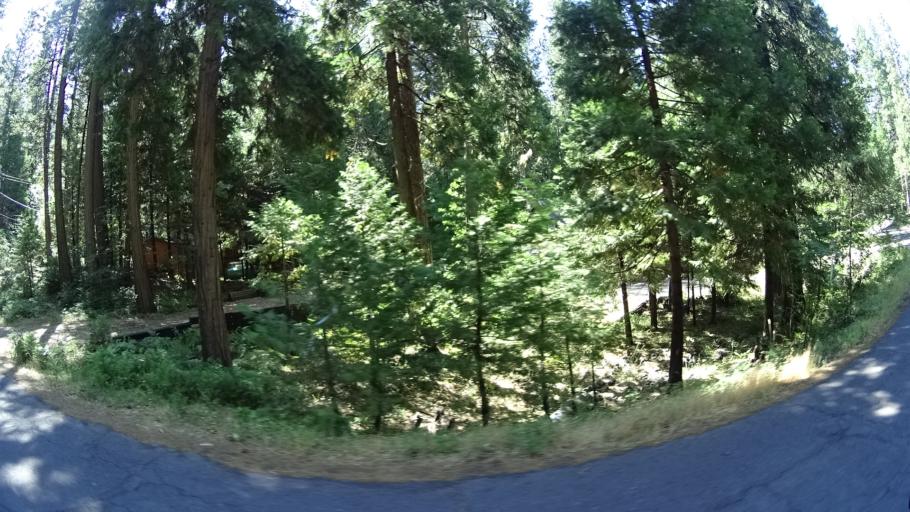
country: US
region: California
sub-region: Calaveras County
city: Arnold
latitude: 38.2442
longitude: -120.3721
